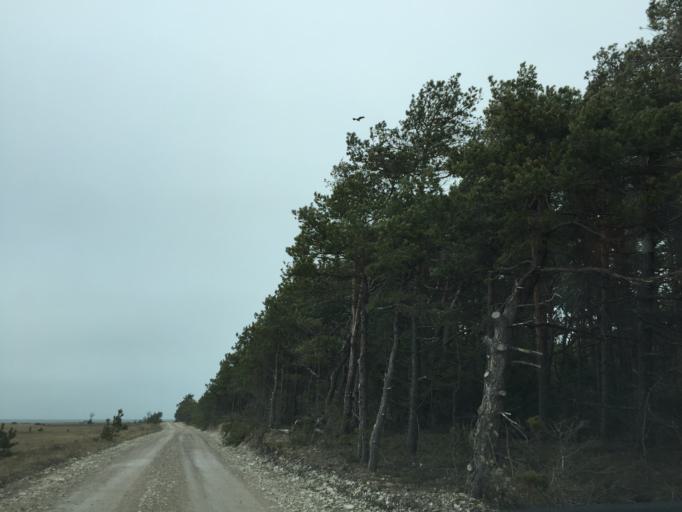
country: EE
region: Saare
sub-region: Kuressaare linn
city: Kuressaare
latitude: 58.5014
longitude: 21.9149
